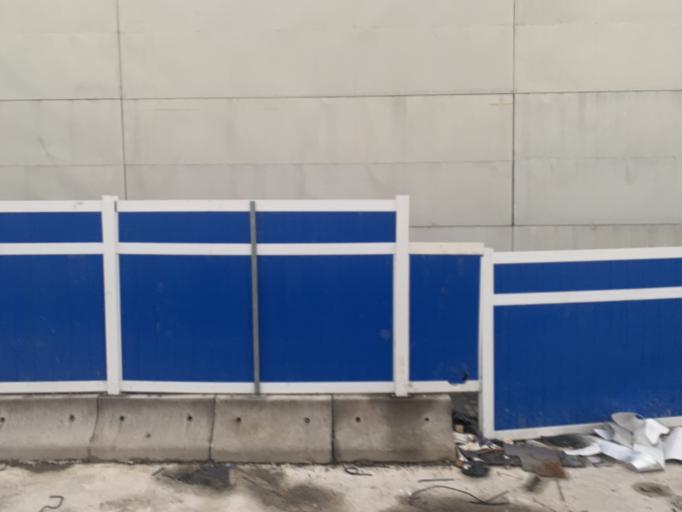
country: CN
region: Shanghai Shi
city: Pudong
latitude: 31.2425
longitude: 121.5375
